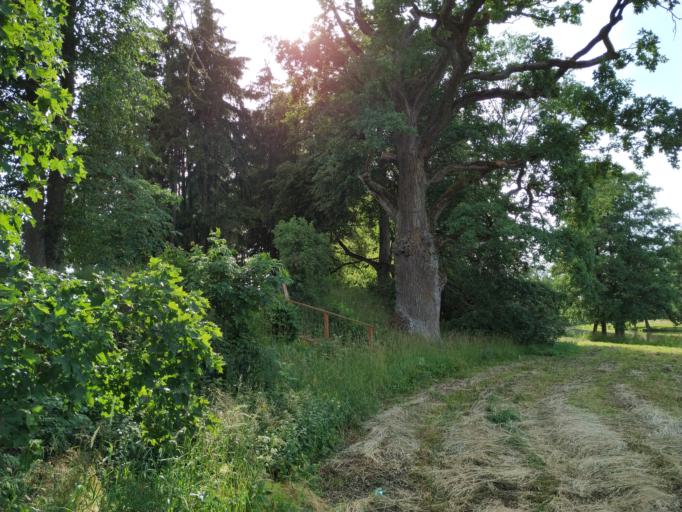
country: LT
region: Panevezys
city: Pasvalys
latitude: 56.1052
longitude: 24.4984
